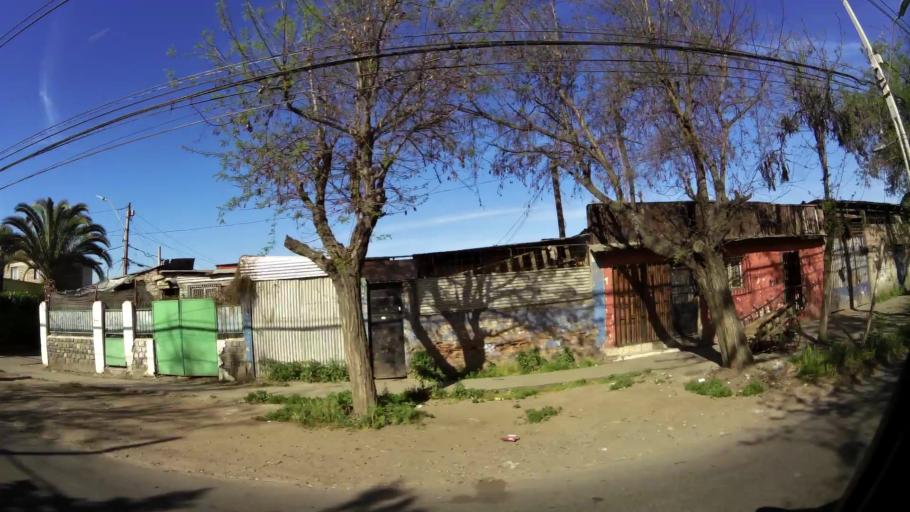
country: CL
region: Santiago Metropolitan
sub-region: Provincia de Santiago
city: Lo Prado
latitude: -33.4648
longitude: -70.6932
